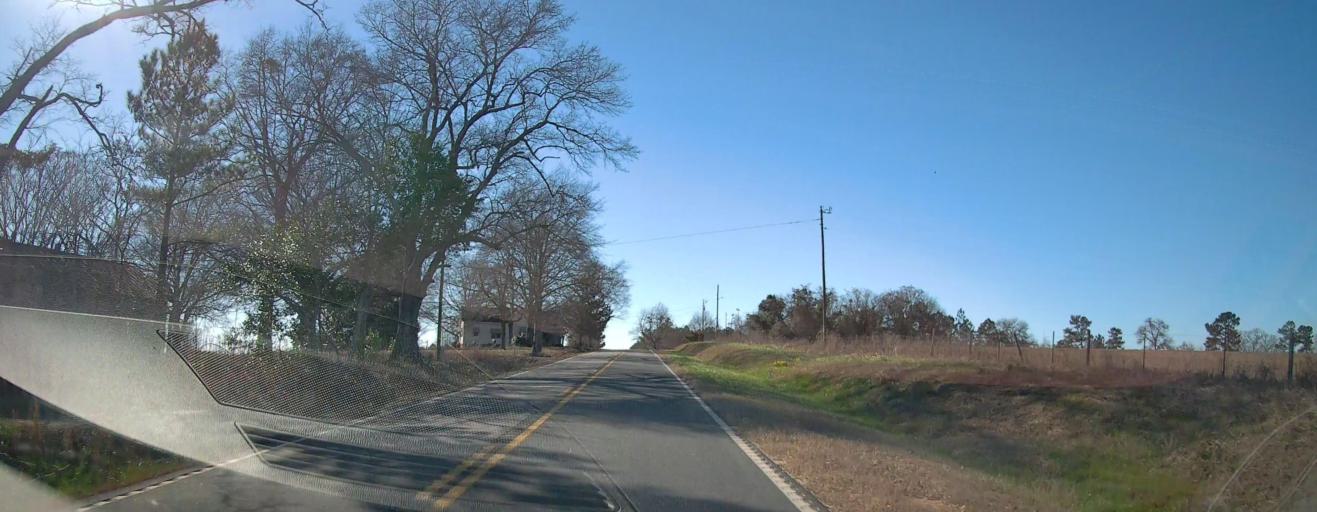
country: US
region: Georgia
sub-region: Taylor County
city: Butler
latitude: 32.6604
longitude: -84.3378
